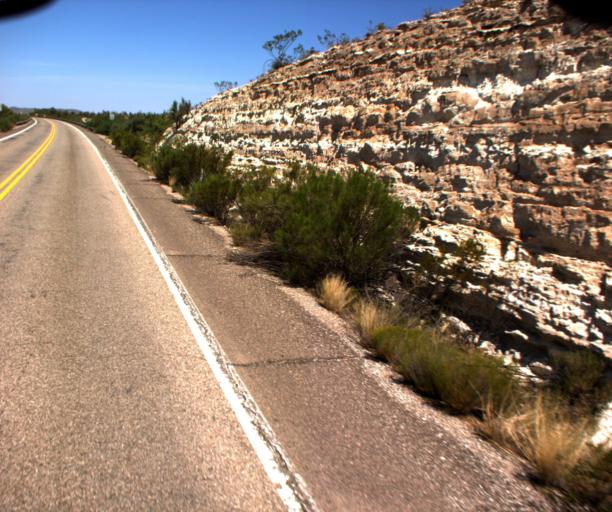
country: US
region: Arizona
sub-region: Gila County
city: Peridot
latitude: 33.2552
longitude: -110.2835
